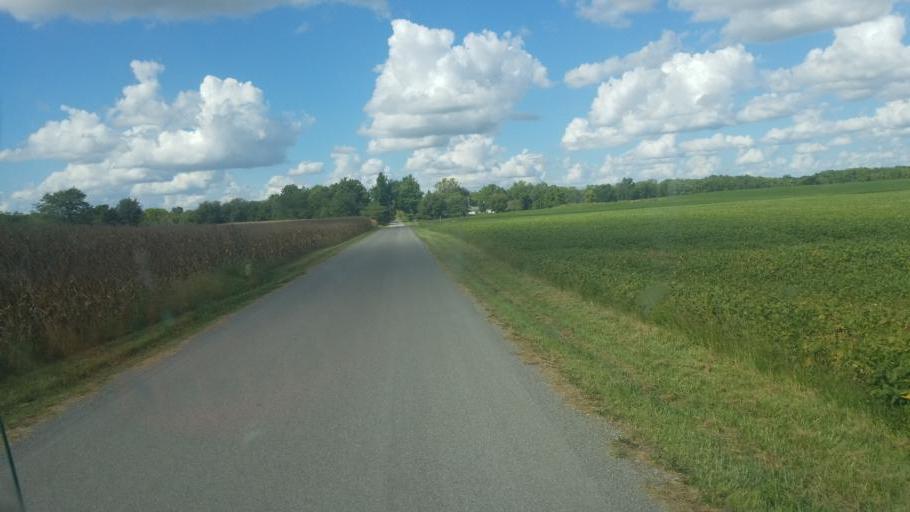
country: US
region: Ohio
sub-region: Hardin County
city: Kenton
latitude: 40.5341
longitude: -83.5426
